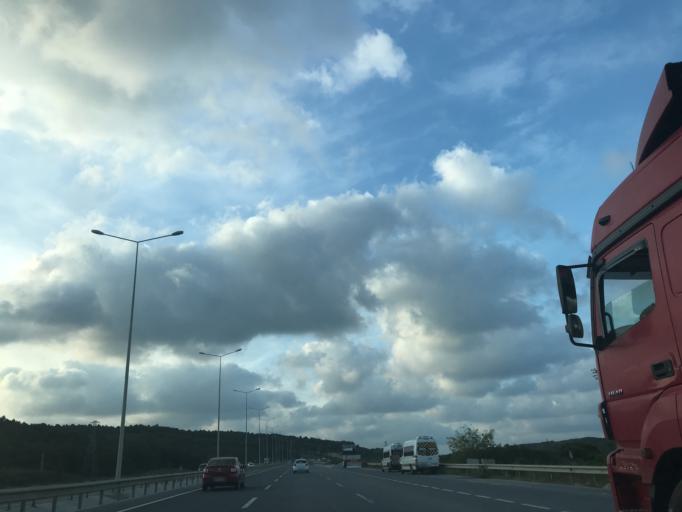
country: TR
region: Istanbul
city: Kemerburgaz
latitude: 41.1820
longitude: 28.8738
